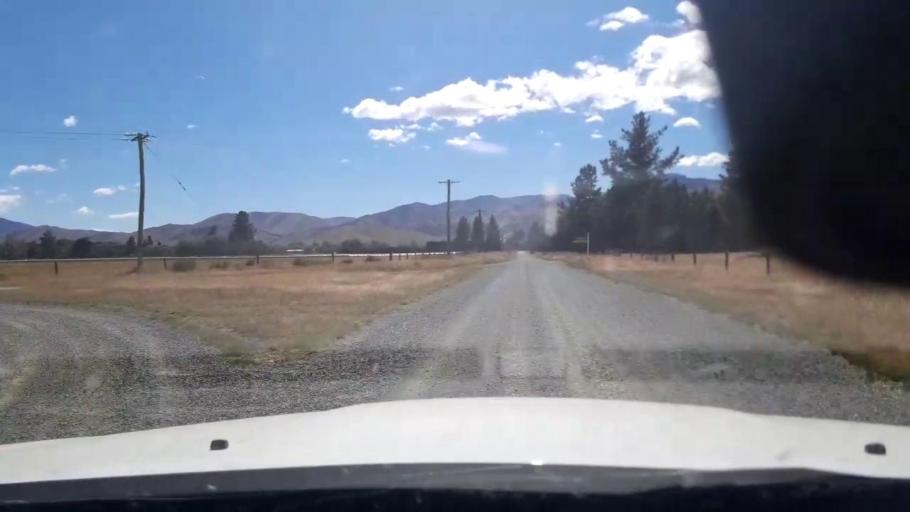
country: NZ
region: Canterbury
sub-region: Timaru District
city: Pleasant Point
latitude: -44.0021
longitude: 170.8366
